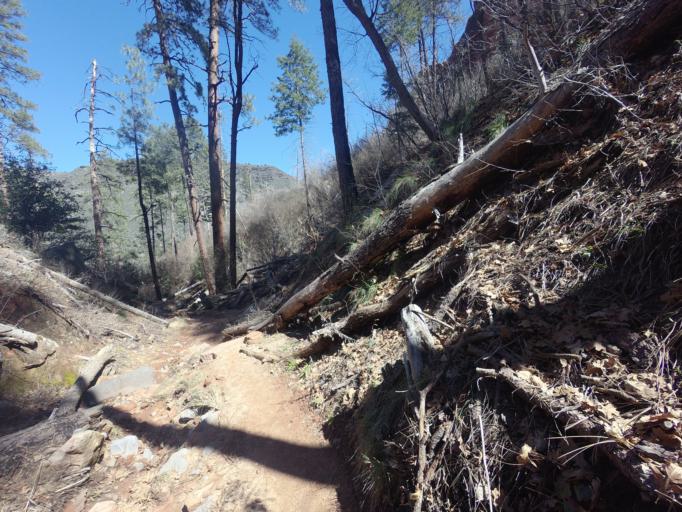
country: US
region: Arizona
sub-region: Coconino County
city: Sedona
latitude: 34.9351
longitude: -111.7500
